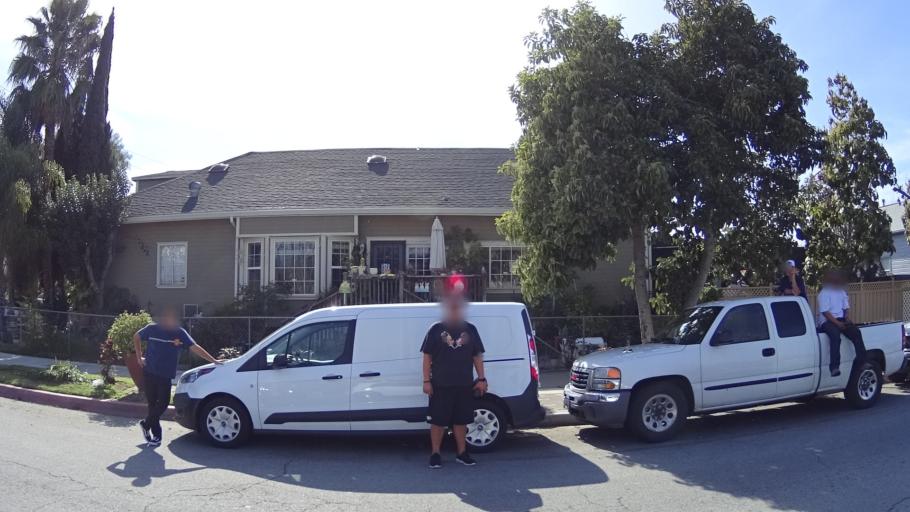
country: US
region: California
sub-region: Santa Clara County
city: San Jose
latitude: 37.3476
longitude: -121.8919
